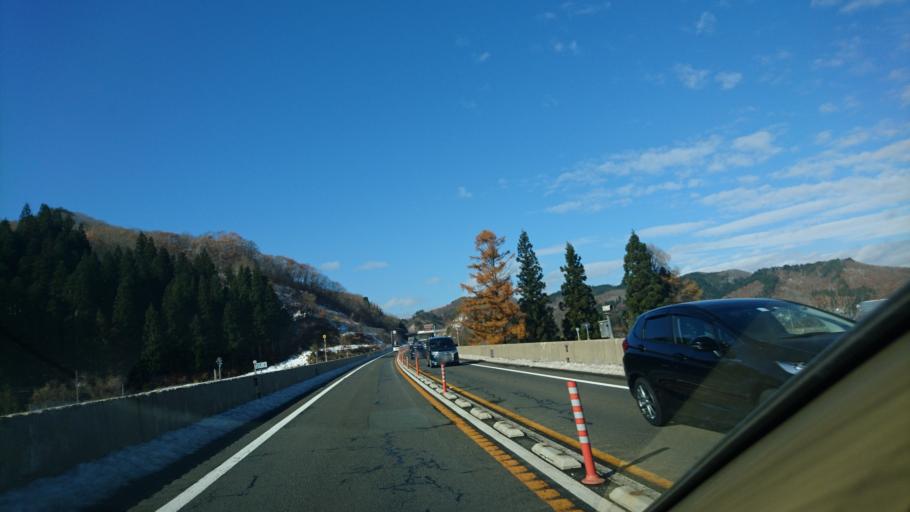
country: JP
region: Akita
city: Yokotemachi
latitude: 39.3070
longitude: 140.7793
